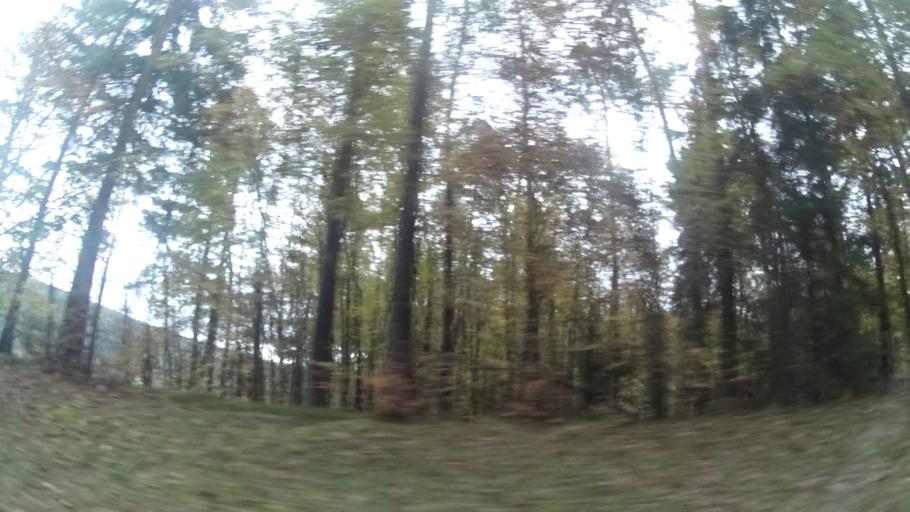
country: DE
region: Bavaria
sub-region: Regierungsbezirk Unterfranken
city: Hohenroth
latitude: 50.3518
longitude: 10.1356
